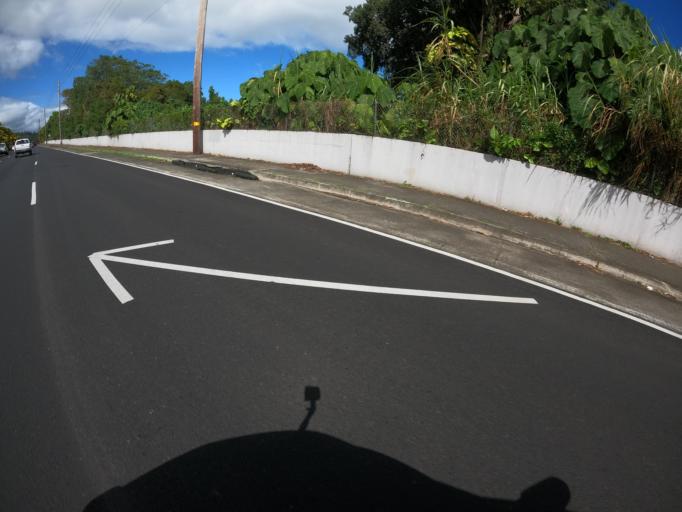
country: US
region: Hawaii
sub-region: Honolulu County
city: Kane'ohe
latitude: 21.4143
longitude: -157.8111
